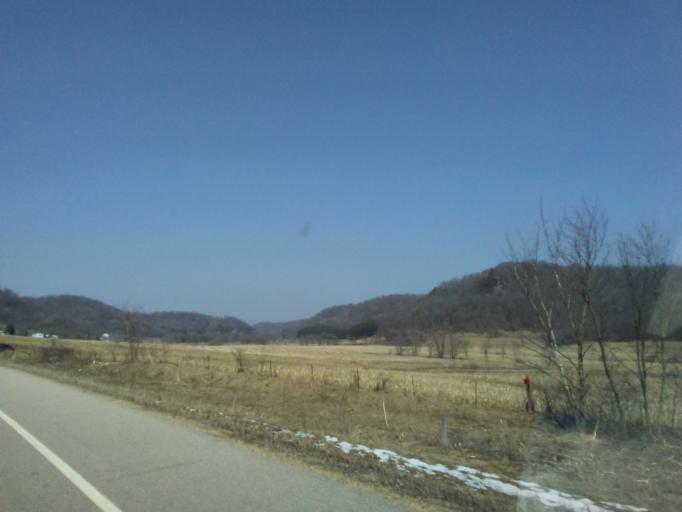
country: US
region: Wisconsin
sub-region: Richland County
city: Richland Center
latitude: 43.3495
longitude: -90.5462
